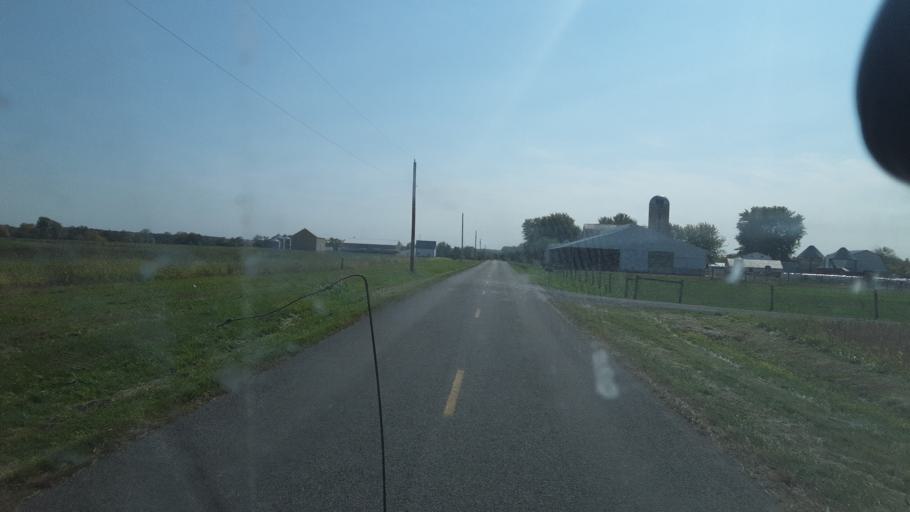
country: US
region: Ohio
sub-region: Logan County
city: Northwood
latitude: 40.5012
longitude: -83.7839
